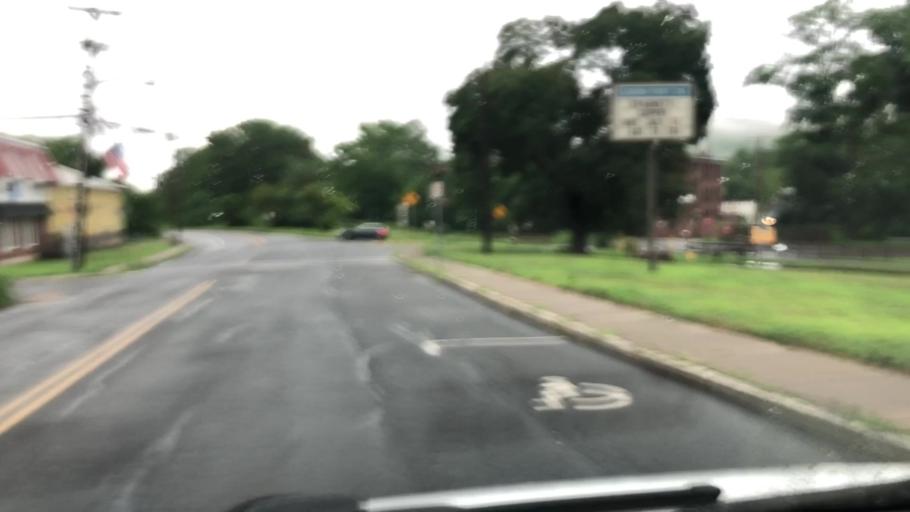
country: US
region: Massachusetts
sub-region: Hampshire County
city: Easthampton
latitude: 42.2759
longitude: -72.6580
